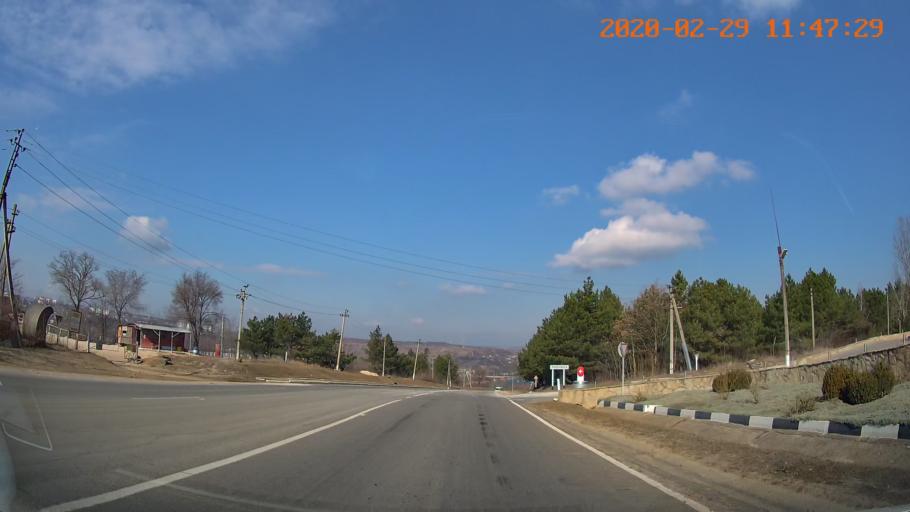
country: MD
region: Rezina
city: Rezina
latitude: 47.7411
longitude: 28.9877
